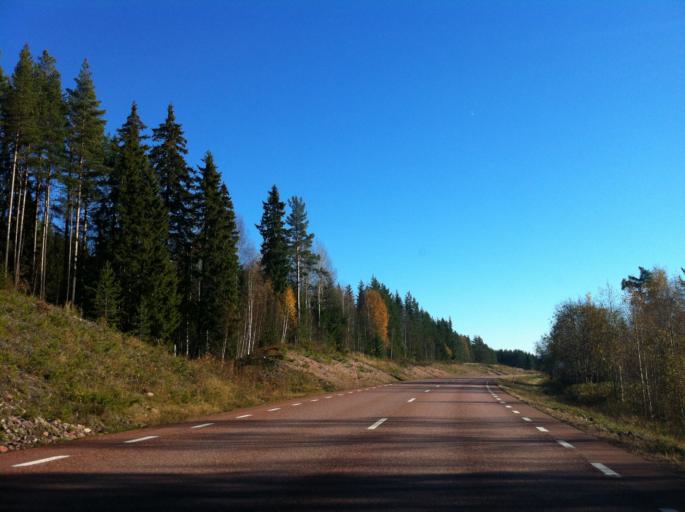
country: SE
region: Dalarna
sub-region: Alvdalens Kommun
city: AElvdalen
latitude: 61.2805
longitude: 13.9493
